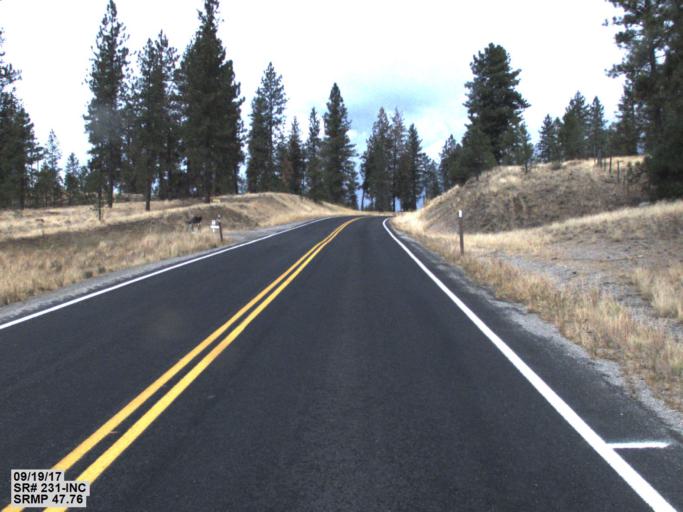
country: US
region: Washington
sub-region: Spokane County
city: Fairchild Air Force Base
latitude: 47.8790
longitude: -117.8390
